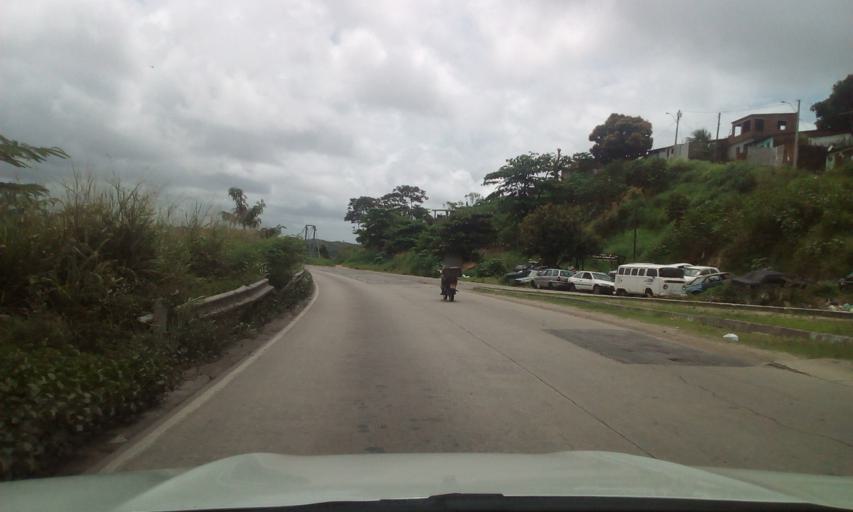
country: BR
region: Pernambuco
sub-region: Jaboatao Dos Guararapes
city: Jaboatao dos Guararapes
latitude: -8.1208
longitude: -34.9429
